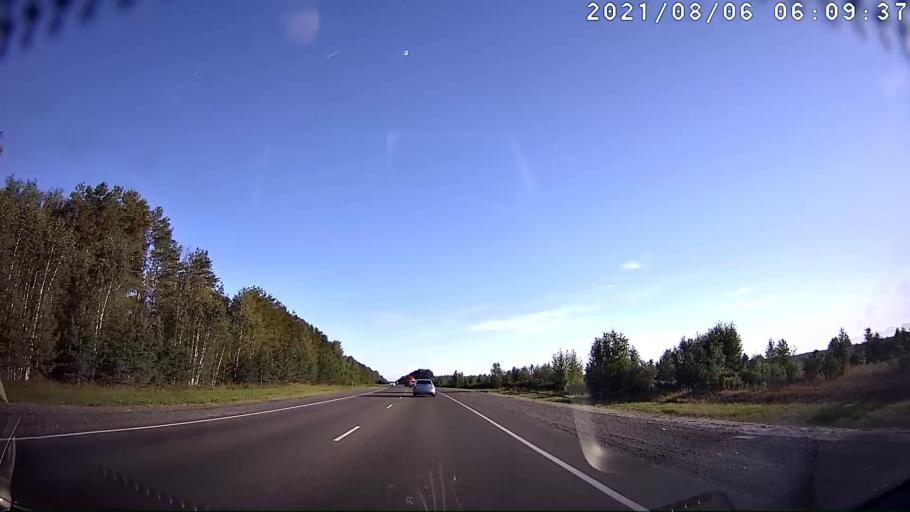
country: RU
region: Mariy-El
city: Pomary
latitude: 55.9260
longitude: 48.3750
